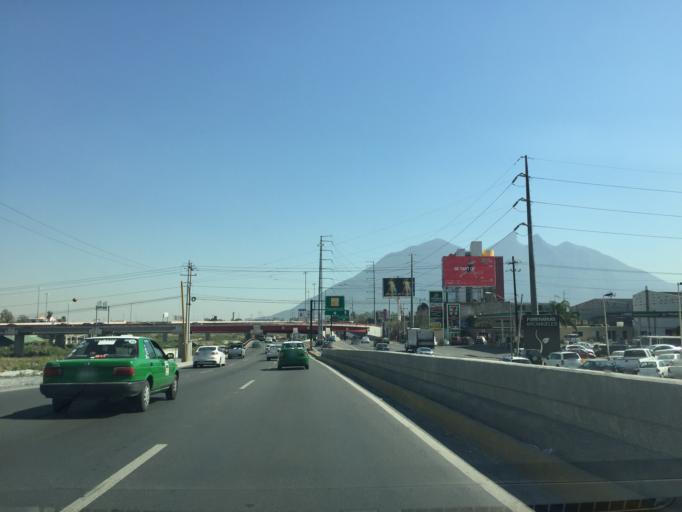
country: MX
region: Nuevo Leon
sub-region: Monterrey
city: Monterrey
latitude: 25.6625
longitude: -100.3148
